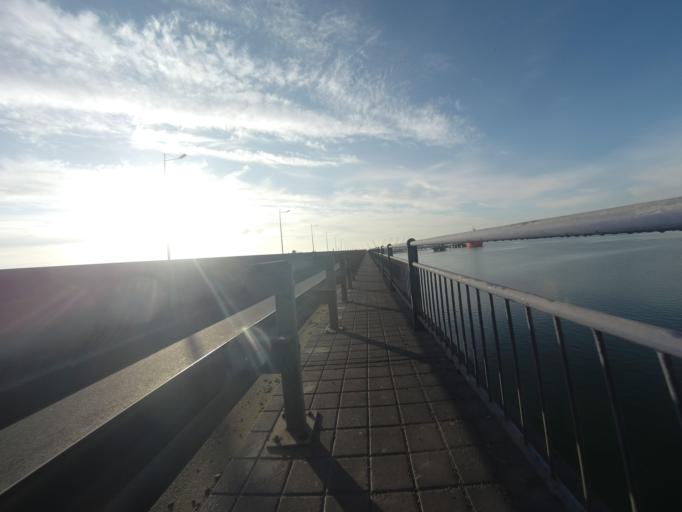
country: ES
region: Andalusia
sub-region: Provincia de Huelva
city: Punta Umbria
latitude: 37.2104
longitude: -6.9380
